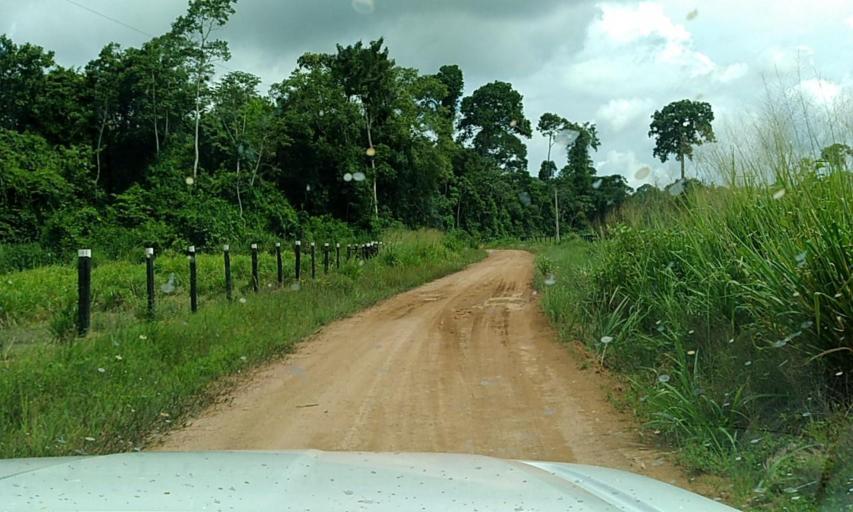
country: BR
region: Para
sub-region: Senador Jose Porfirio
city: Senador Jose Porfirio
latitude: -2.5164
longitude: -51.8390
